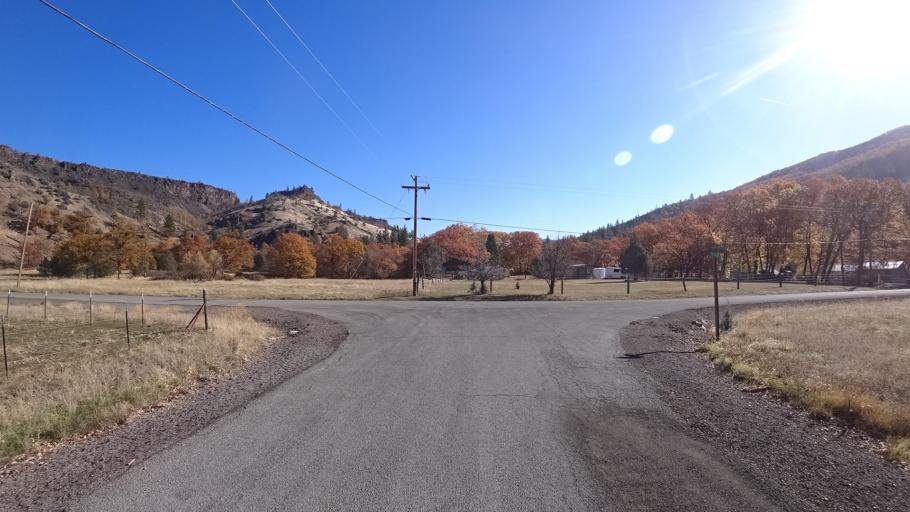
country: US
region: California
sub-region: Siskiyou County
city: Montague
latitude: 41.9661
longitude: -122.2609
